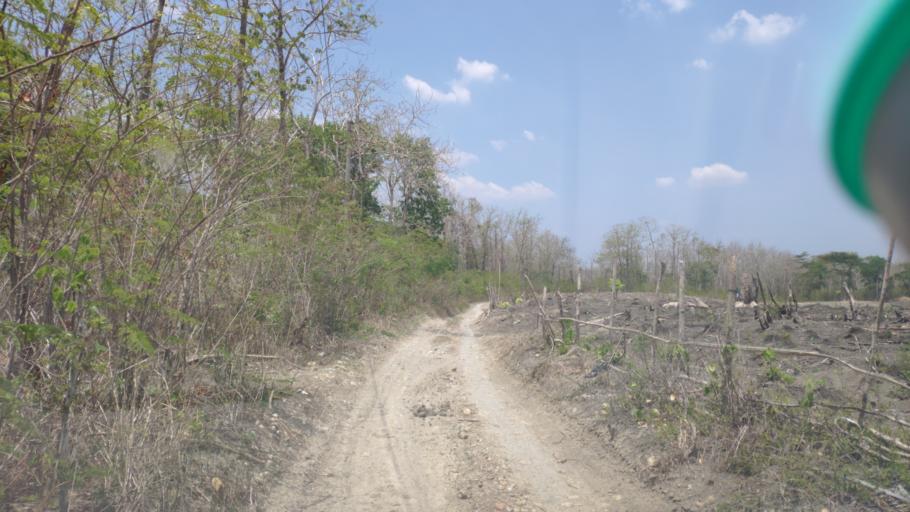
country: ID
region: Central Java
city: Randublatung
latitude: -7.2700
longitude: 111.3313
